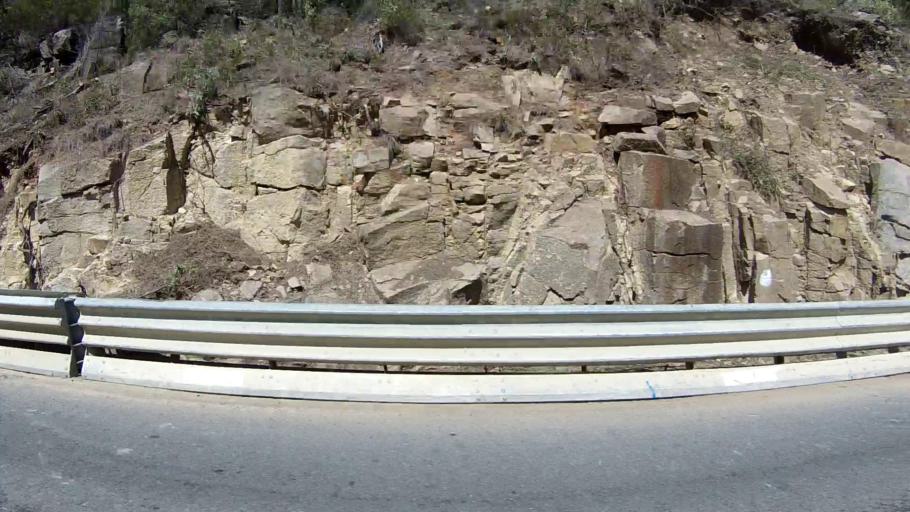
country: AU
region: Tasmania
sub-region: Sorell
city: Sorell
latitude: -42.5606
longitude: 147.8550
